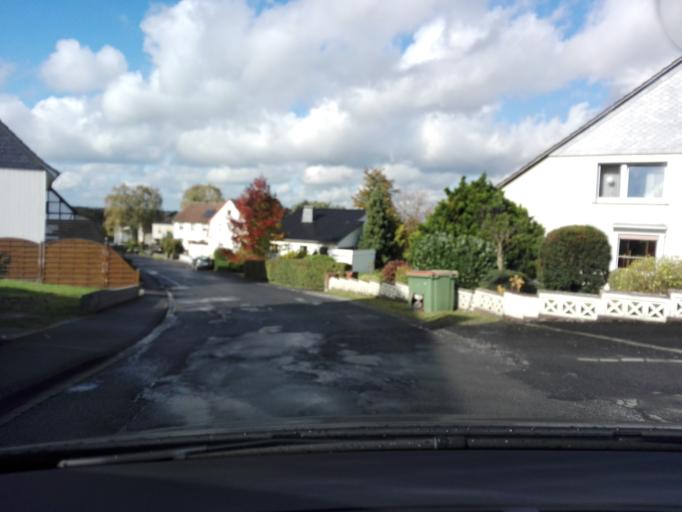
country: DE
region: North Rhine-Westphalia
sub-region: Regierungsbezirk Arnsberg
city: Holzwickede
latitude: 51.5012
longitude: 7.6574
